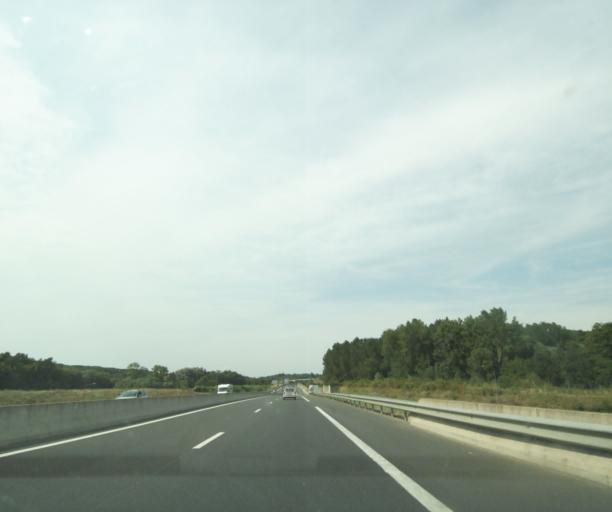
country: FR
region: Centre
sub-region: Departement d'Indre-et-Loire
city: La Membrolle-sur-Choisille
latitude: 47.4176
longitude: 0.6359
